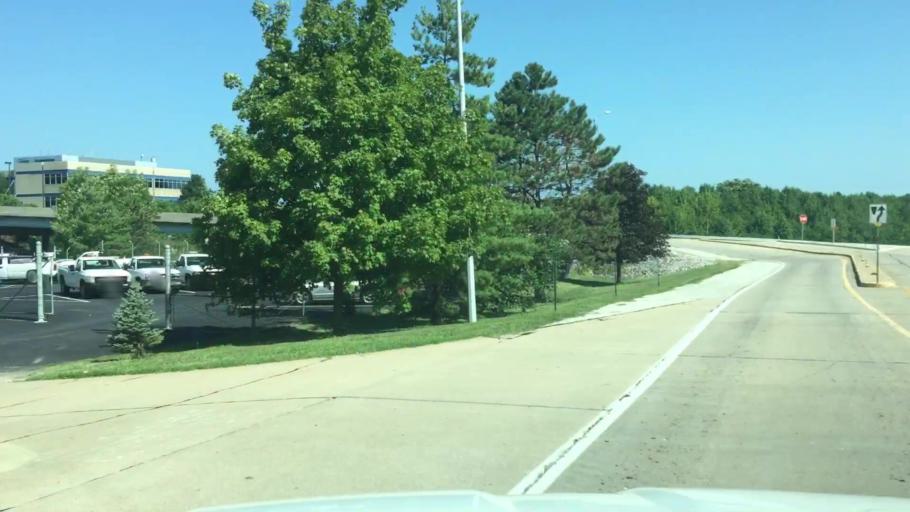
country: US
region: Missouri
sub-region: Saint Louis County
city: Manchester
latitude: 38.6393
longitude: -90.5105
